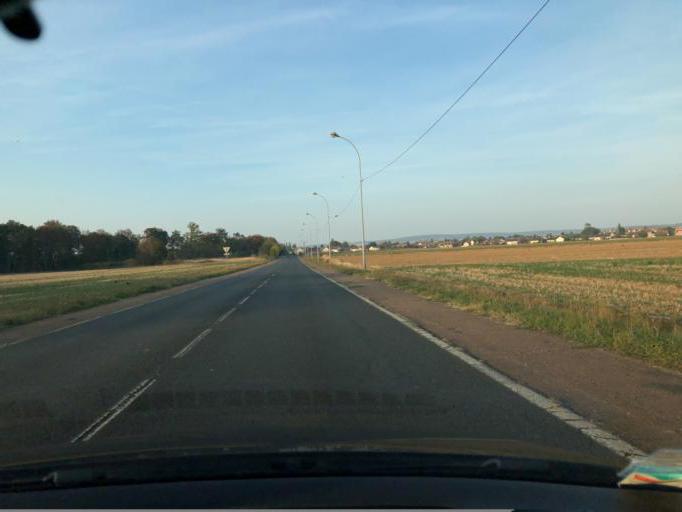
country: FR
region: Bourgogne
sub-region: Departement de l'Yonne
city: Saint-Clement
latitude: 48.2088
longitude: 3.2929
